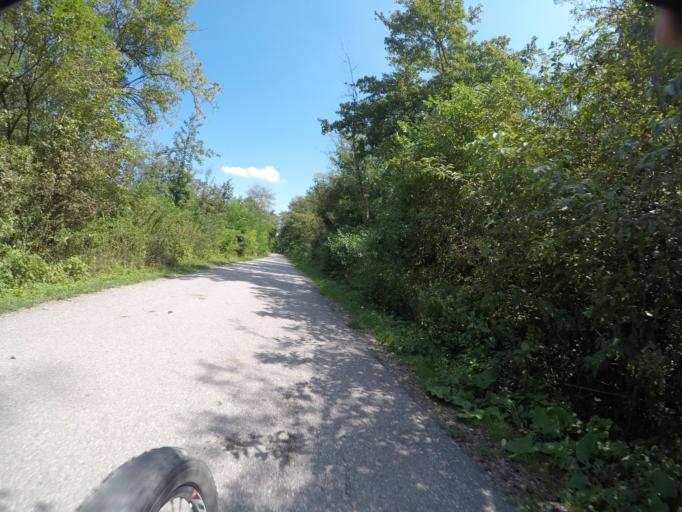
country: AT
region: Lower Austria
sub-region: Politischer Bezirk Ganserndorf
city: Gross-Enzersdorf
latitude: 48.1898
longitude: 16.5358
